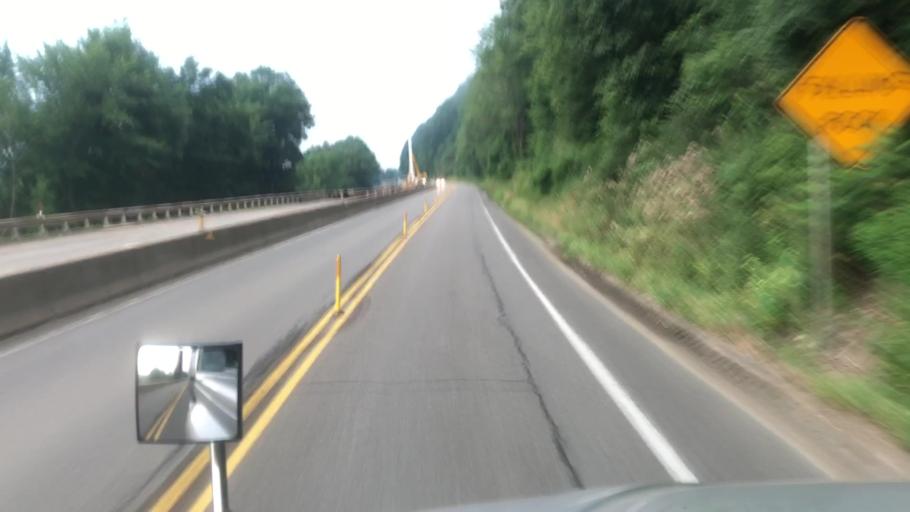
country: US
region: Pennsylvania
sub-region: Venango County
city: Woodland Heights
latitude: 41.4196
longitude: -79.7311
